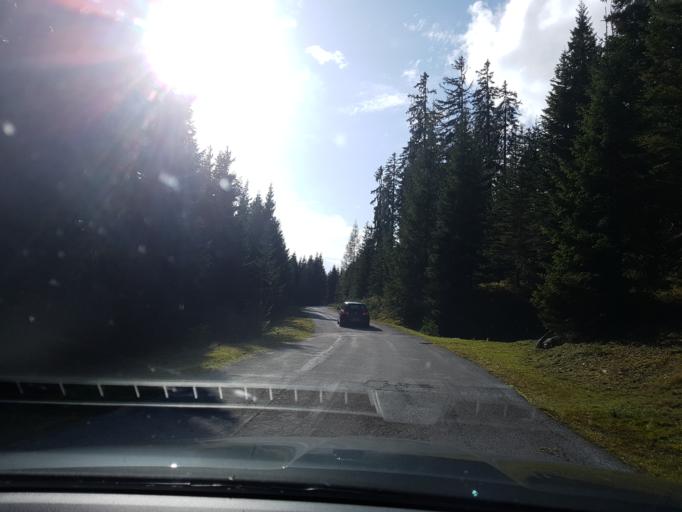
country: AT
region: Salzburg
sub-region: Politischer Bezirk Sankt Johann im Pongau
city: Filzmoos
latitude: 47.4076
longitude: 13.4929
